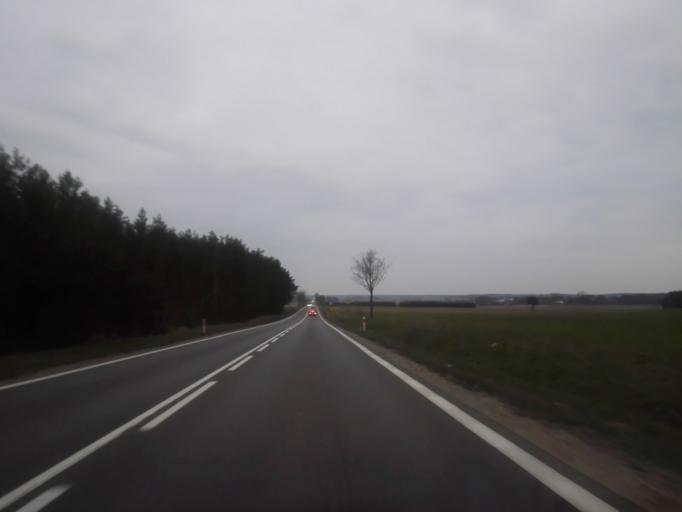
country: PL
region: Podlasie
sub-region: Powiat kolnenski
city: Stawiski
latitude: 53.4347
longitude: 22.1731
